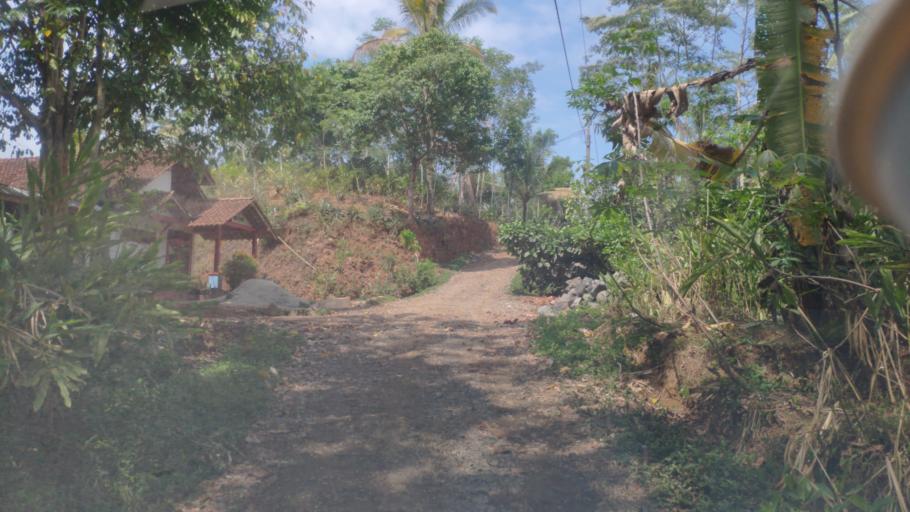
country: ID
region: Central Java
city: Purbalingga
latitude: -7.3432
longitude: 109.6073
